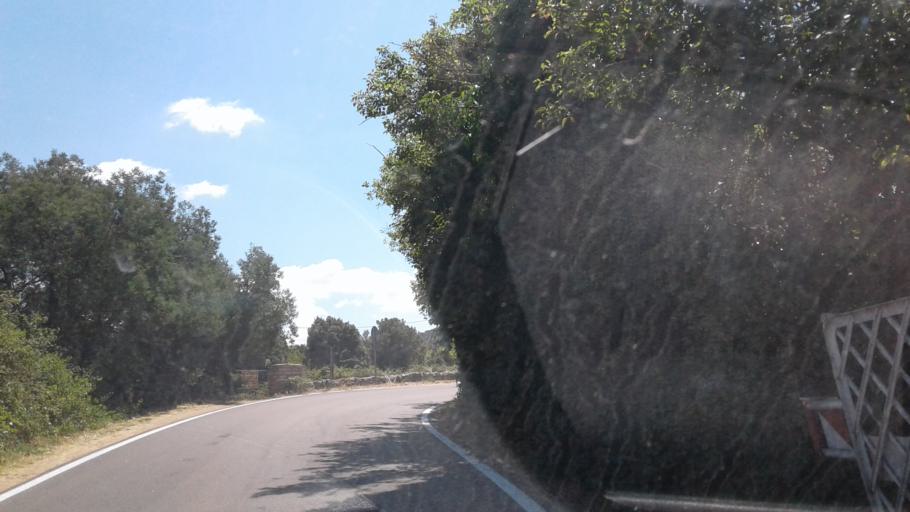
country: IT
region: Sardinia
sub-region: Provincia di Olbia-Tempio
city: Luras
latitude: 40.9230
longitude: 9.1789
